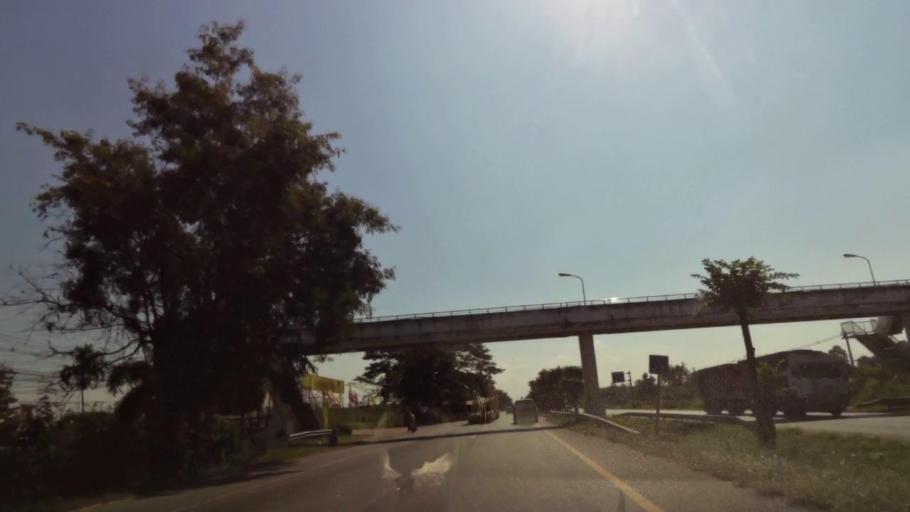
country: TH
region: Nakhon Sawan
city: Kao Liao
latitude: 15.7940
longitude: 100.1208
